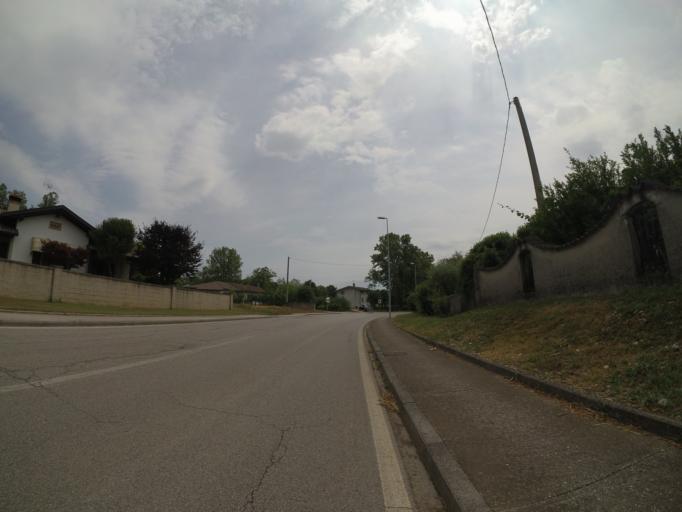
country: IT
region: Friuli Venezia Giulia
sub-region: Provincia di Udine
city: Sedegliano
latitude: 46.0092
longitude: 12.9805
